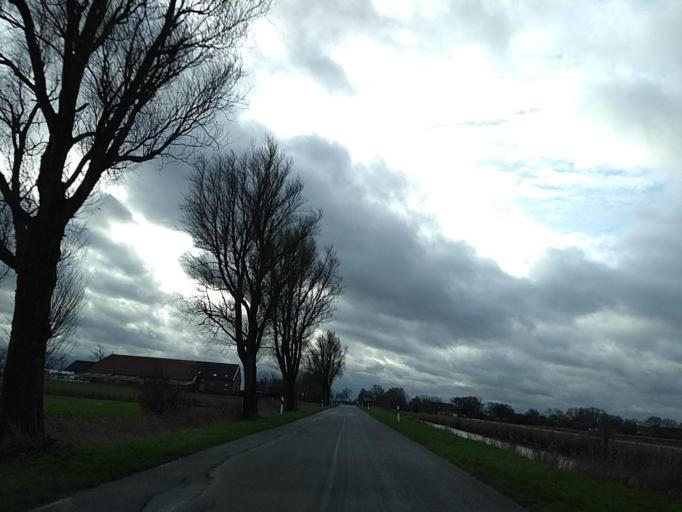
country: DE
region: Lower Saxony
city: Emden
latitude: 53.3047
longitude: 7.2509
